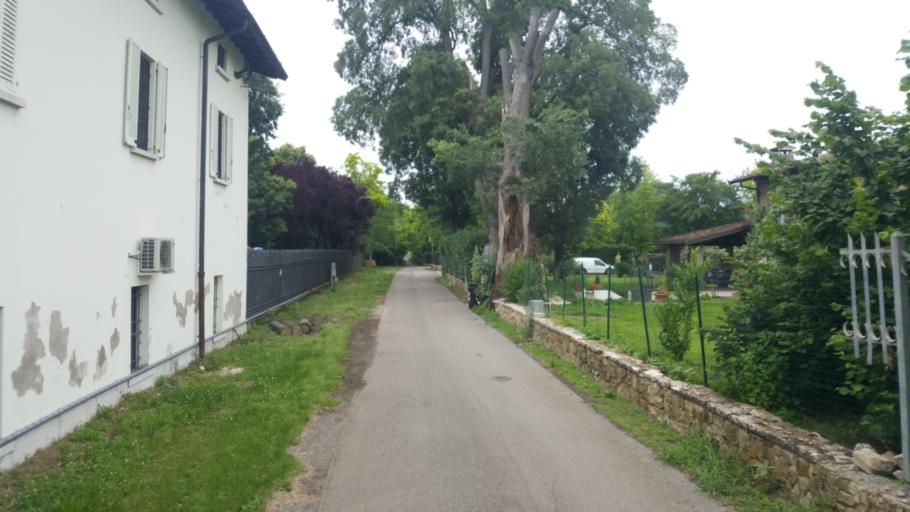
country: IT
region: Lombardy
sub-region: Provincia di Brescia
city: Molinetto
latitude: 45.4890
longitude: 10.3711
